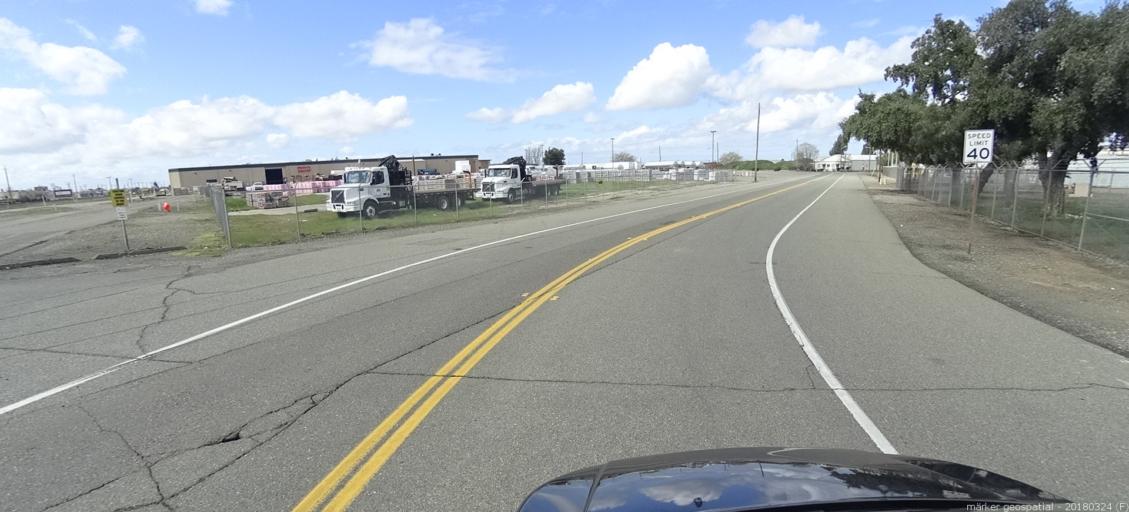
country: US
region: California
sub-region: Sacramento County
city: North Highlands
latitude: 38.6518
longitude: -121.3919
